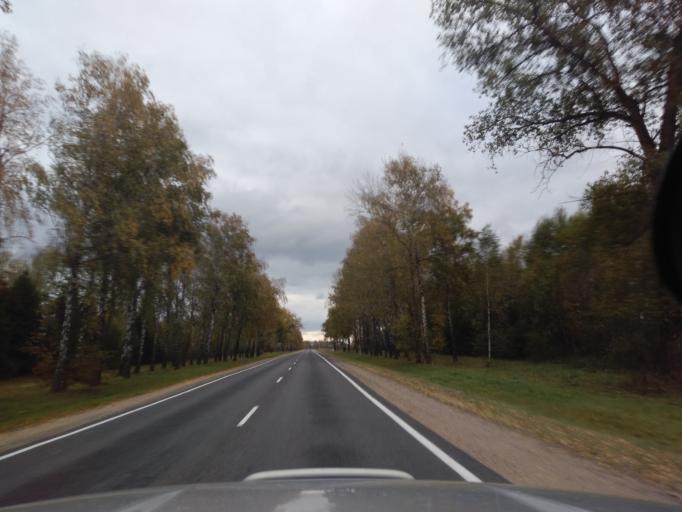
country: BY
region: Minsk
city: Slutsk
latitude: 53.2196
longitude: 27.5345
